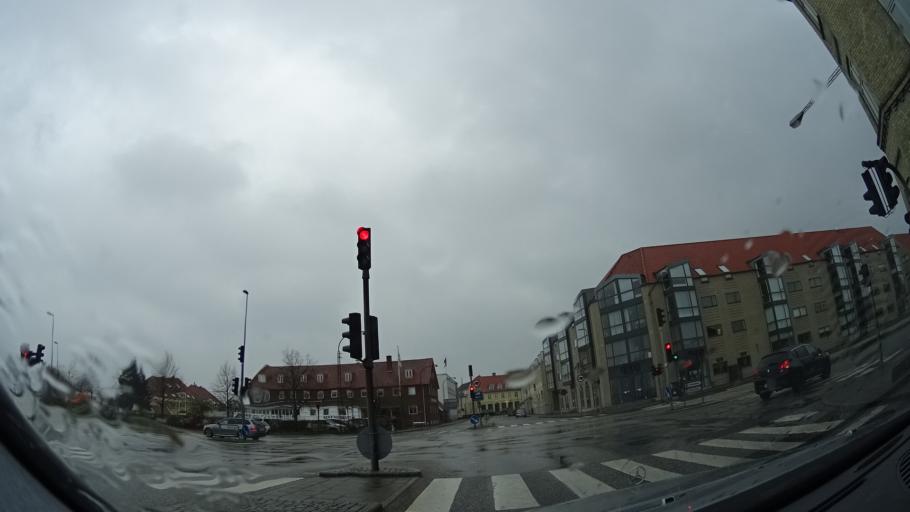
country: DK
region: Zealand
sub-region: Holbaek Kommune
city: Holbaek
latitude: 55.7188
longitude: 11.7059
